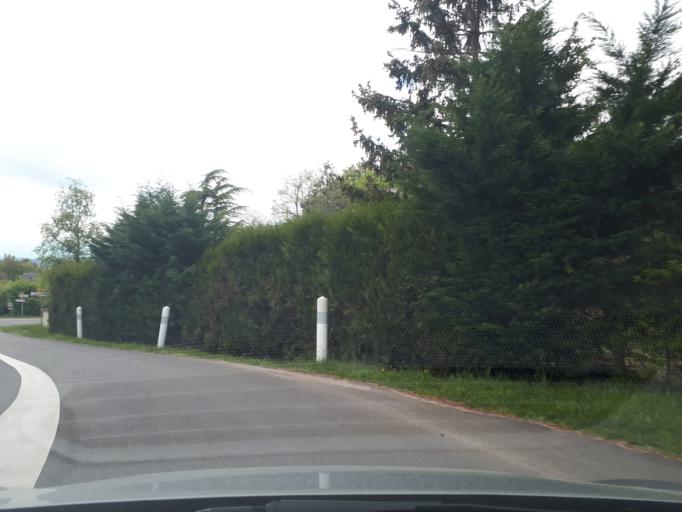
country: FR
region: Rhone-Alpes
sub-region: Departement de la Loire
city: Civens
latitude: 45.7624
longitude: 4.2688
